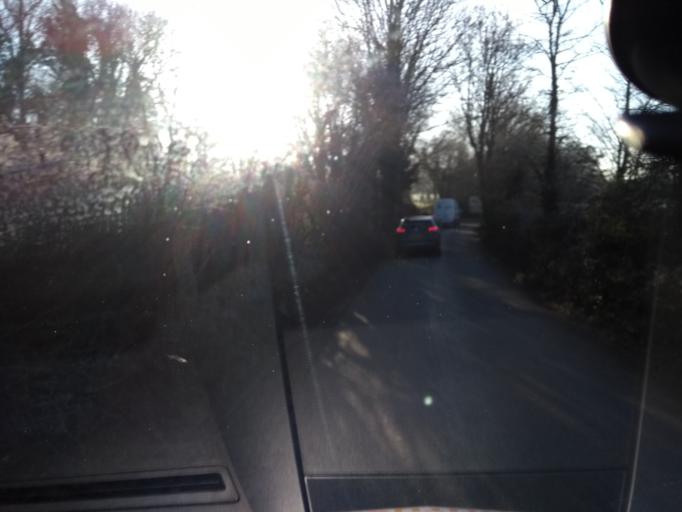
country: GB
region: England
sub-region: Somerset
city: Bruton
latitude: 51.1189
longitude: -2.4558
